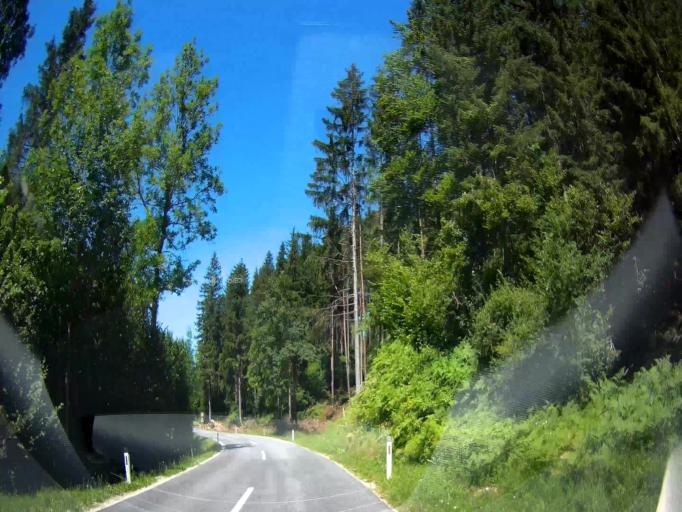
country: AT
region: Carinthia
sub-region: Politischer Bezirk Klagenfurt Land
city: Ferlach
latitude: 46.5129
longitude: 14.2936
